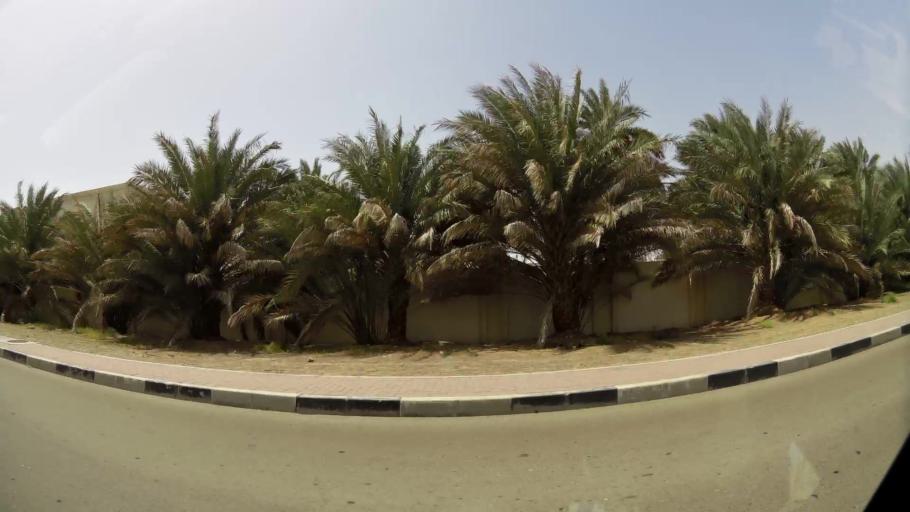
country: AE
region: Abu Dhabi
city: Al Ain
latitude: 24.1810
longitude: 55.7084
